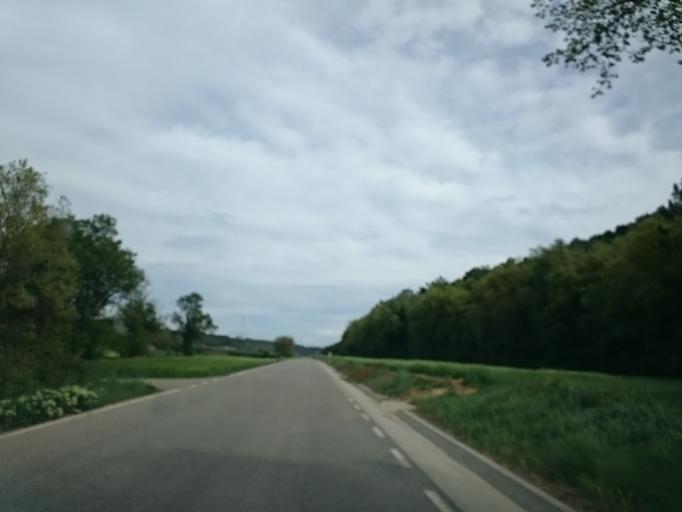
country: ES
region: Catalonia
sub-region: Provincia de Barcelona
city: Pujalt
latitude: 41.7279
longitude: 1.4083
